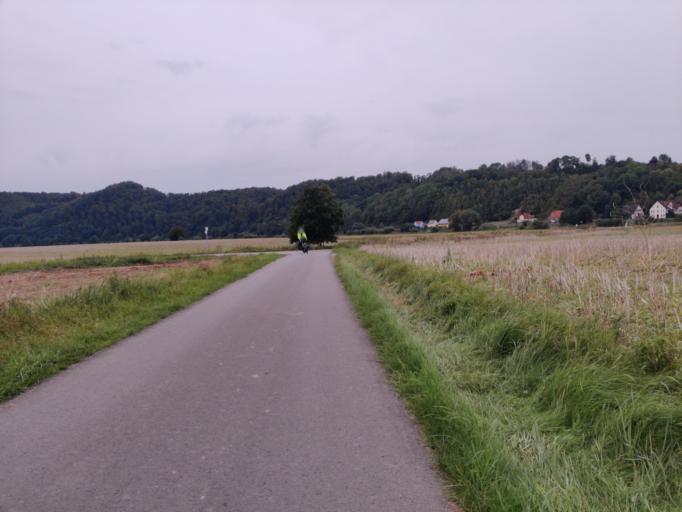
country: DE
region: Lower Saxony
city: Brevorde
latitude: 51.9085
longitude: 9.4270
